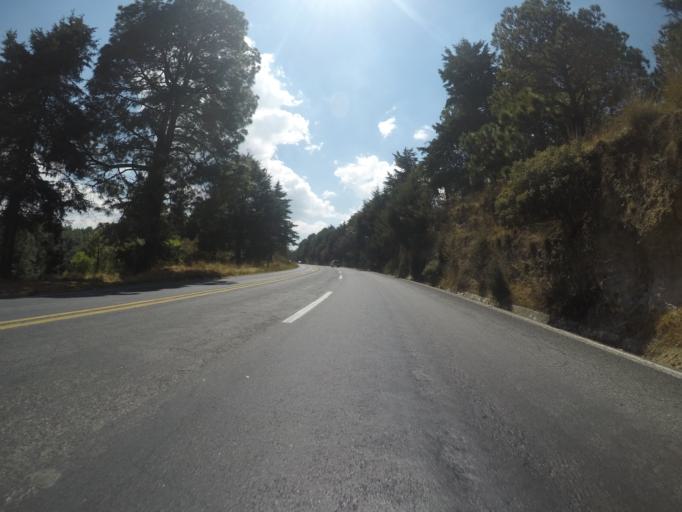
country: MX
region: Mexico
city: San Juan de las Huertas
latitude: 19.2231
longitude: -99.7931
